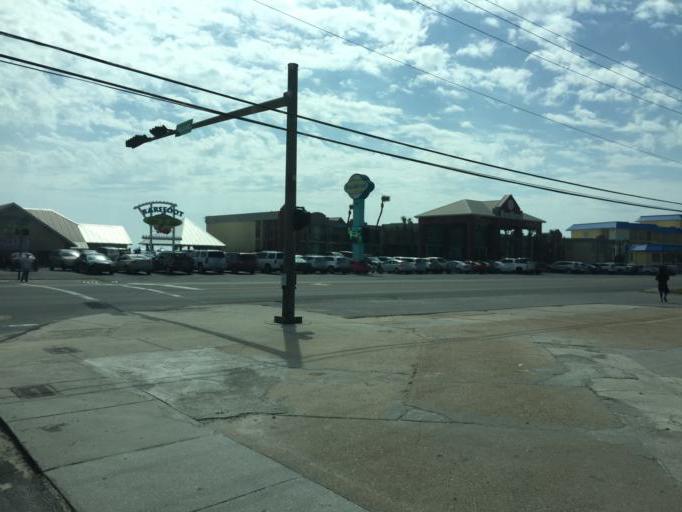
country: US
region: Florida
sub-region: Bay County
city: Laguna Beach
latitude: 30.2103
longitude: -85.8659
